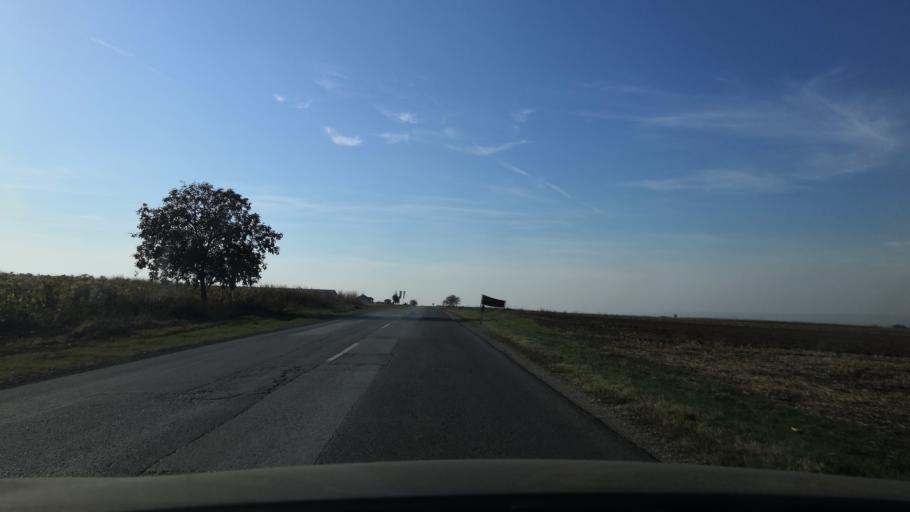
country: RS
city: Putinci
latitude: 45.0038
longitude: 19.9219
